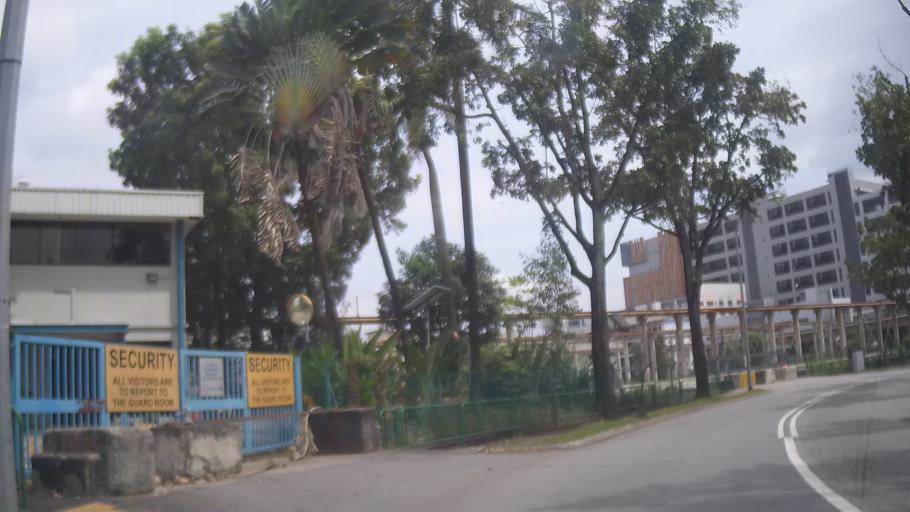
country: MY
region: Johor
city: Johor Bahru
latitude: 1.4091
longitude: 103.7479
